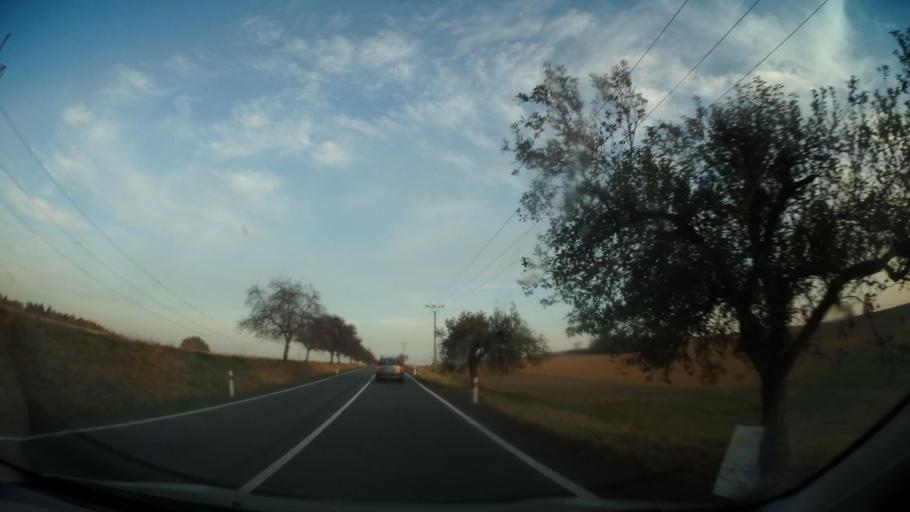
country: CZ
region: Central Bohemia
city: Trhovy Stepanov
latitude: 49.6631
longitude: 14.9851
